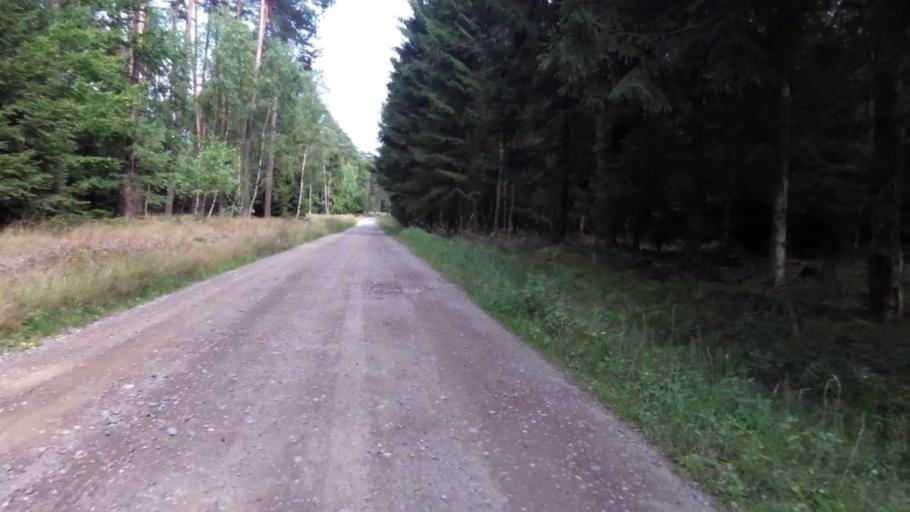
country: PL
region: West Pomeranian Voivodeship
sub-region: Powiat drawski
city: Zlocieniec
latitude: 53.5628
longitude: 15.9479
